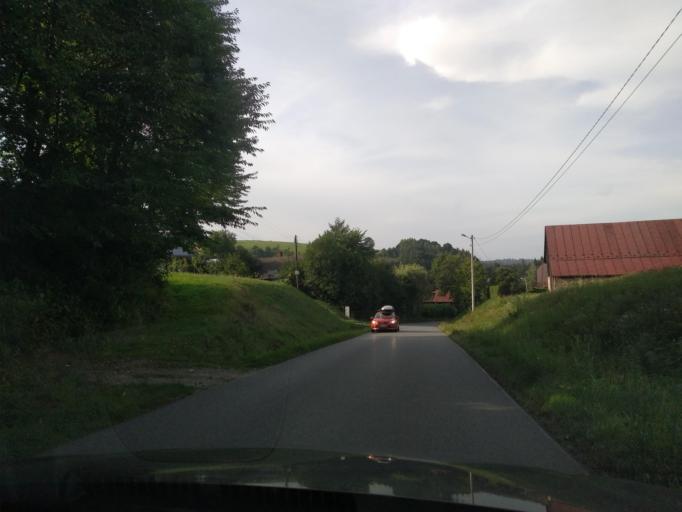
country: PL
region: Subcarpathian Voivodeship
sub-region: Powiat brzozowski
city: Dydnia
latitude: 49.6805
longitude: 22.1845
